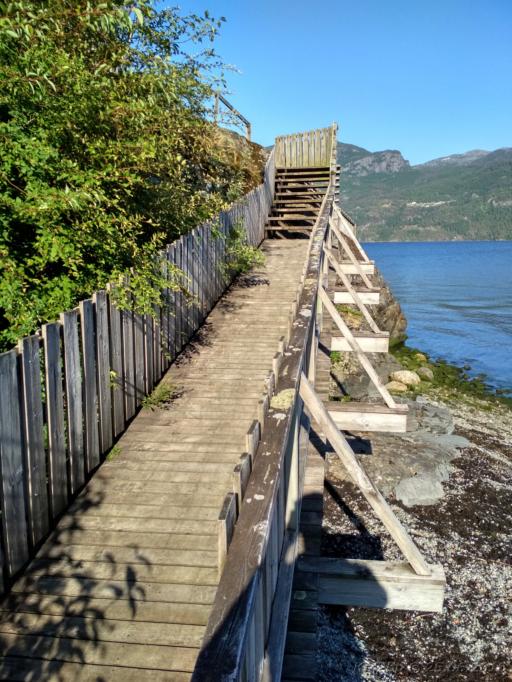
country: NO
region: Rogaland
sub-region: Sauda
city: Sauda
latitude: 59.6397
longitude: 6.3104
